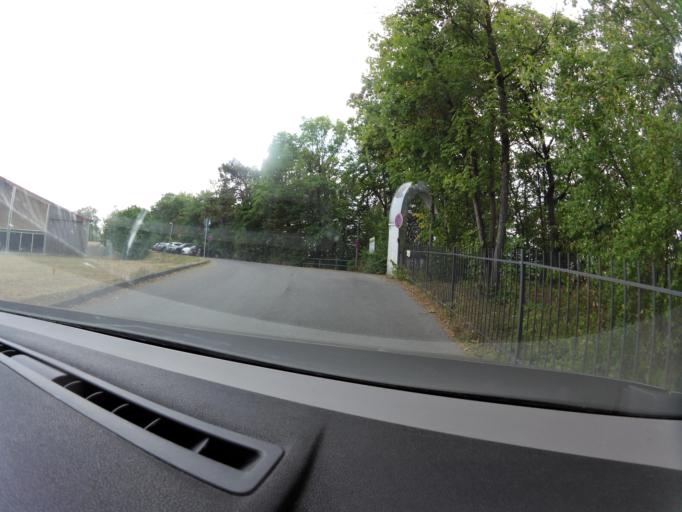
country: DE
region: Bavaria
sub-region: Regierungsbezirk Unterfranken
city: Bad Kissingen
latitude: 50.1918
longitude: 10.0871
